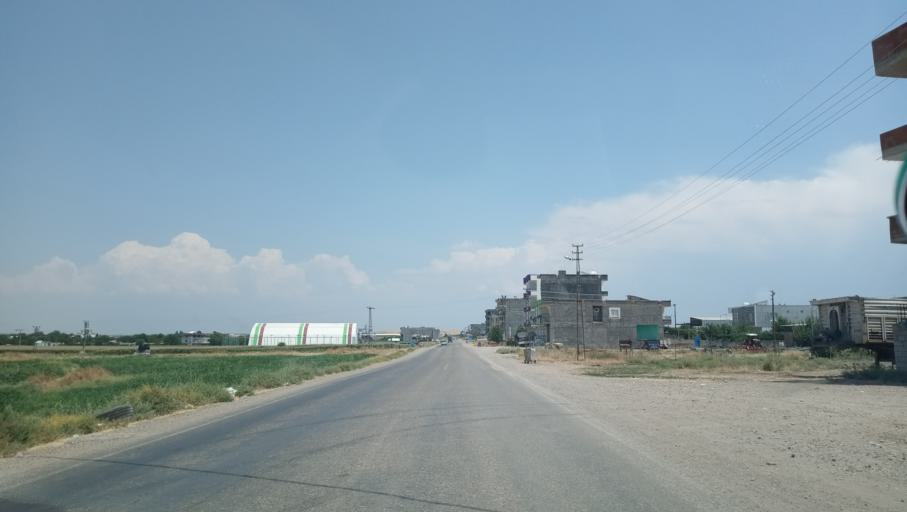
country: TR
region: Diyarbakir
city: Aralik
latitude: 37.8285
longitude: 40.6722
